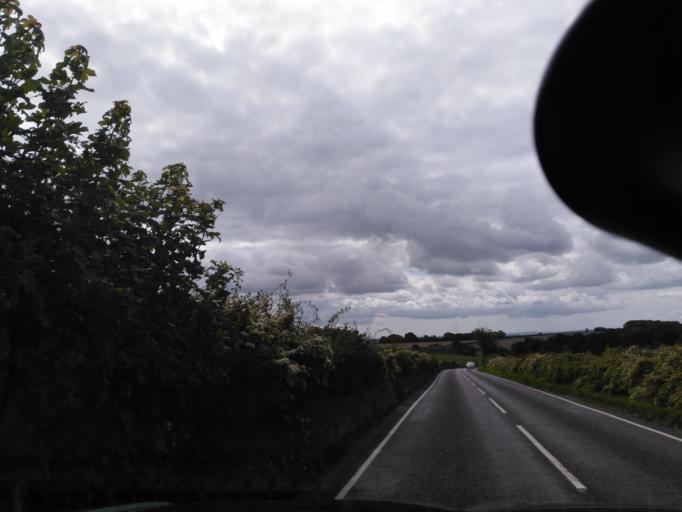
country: GB
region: England
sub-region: Dorset
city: Blandford Forum
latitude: 50.9062
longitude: -2.1583
